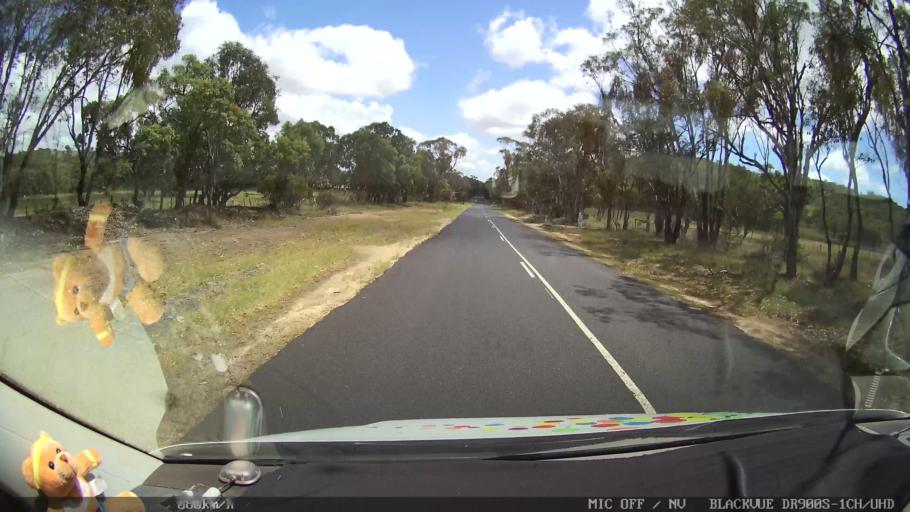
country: AU
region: New South Wales
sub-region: Glen Innes Severn
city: Glen Innes
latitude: -29.5379
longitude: 151.6730
